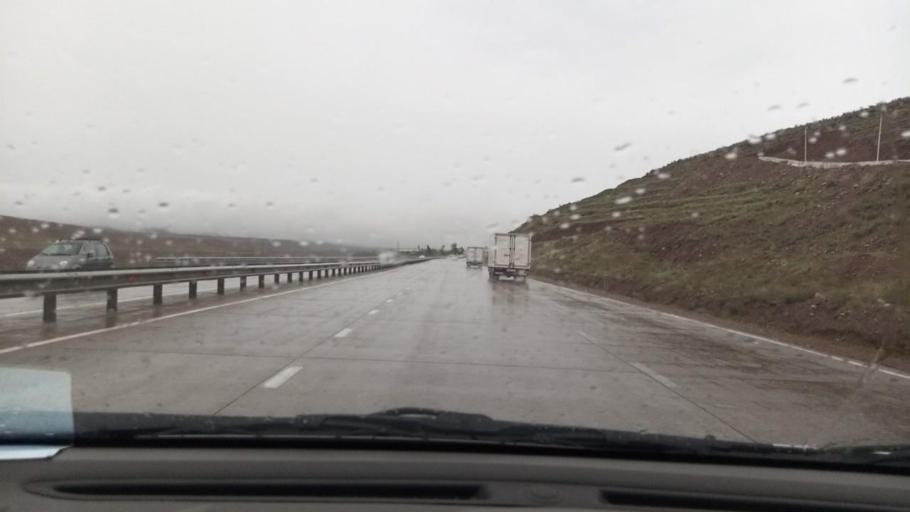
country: UZ
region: Namangan
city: Pop Shahri
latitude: 40.9256
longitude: 70.7226
